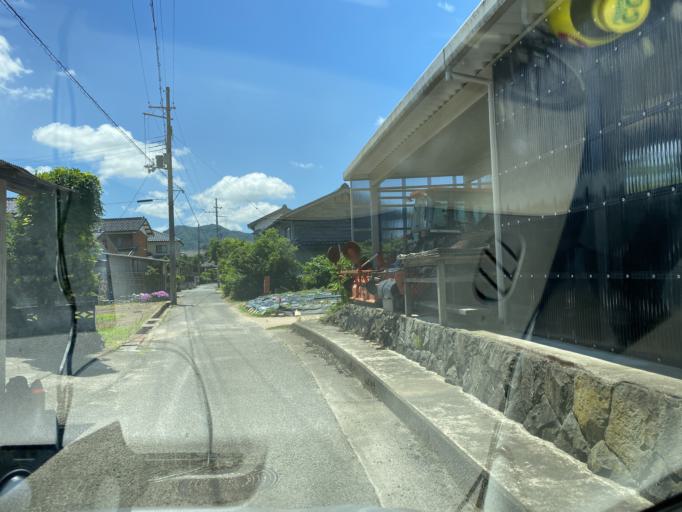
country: JP
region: Hyogo
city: Toyooka
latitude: 35.4906
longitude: 134.8072
